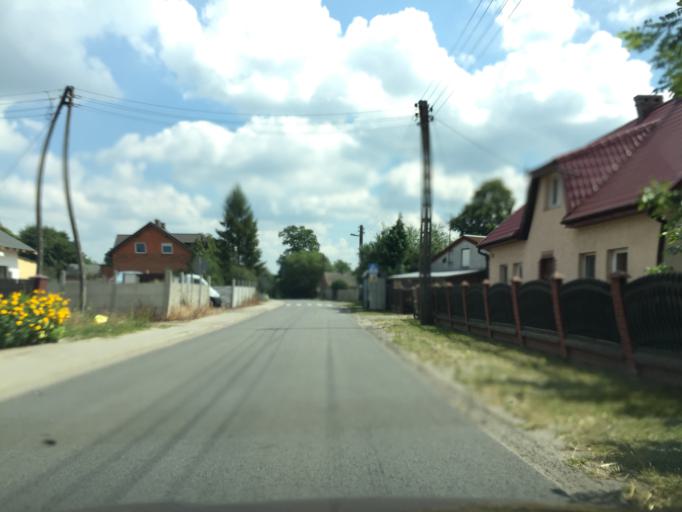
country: PL
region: Greater Poland Voivodeship
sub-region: Powiat kaliski
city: Zelazkow
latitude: 51.9433
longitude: 18.2079
